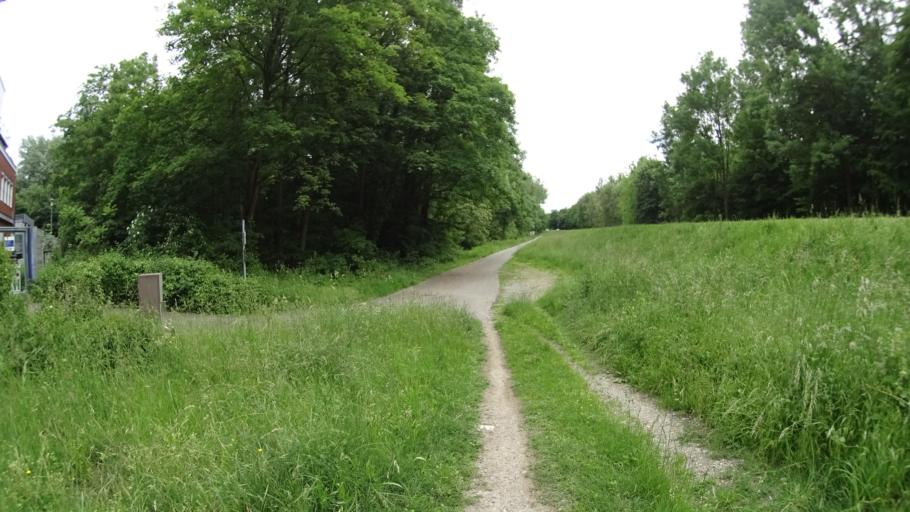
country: DE
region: Baden-Wuerttemberg
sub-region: Karlsruhe Region
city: Rheinstetten
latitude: 49.0097
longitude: 8.3077
